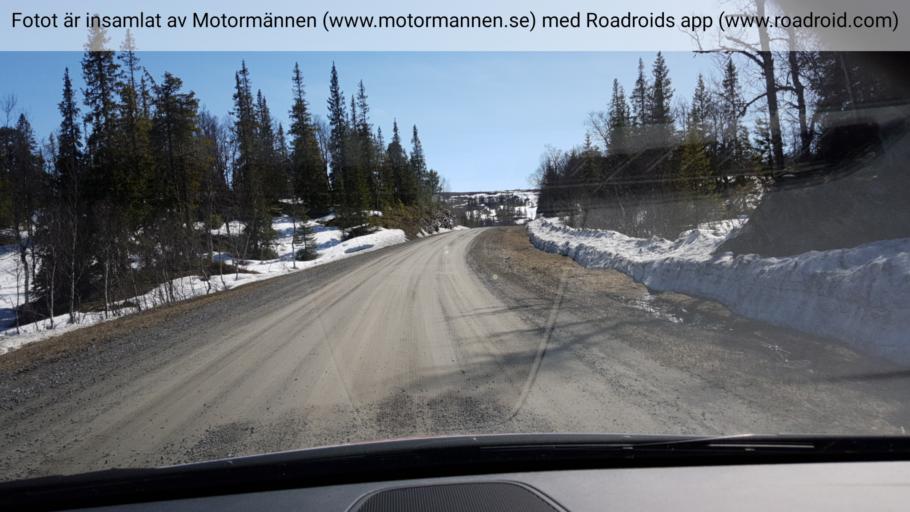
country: NO
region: Nord-Trondelag
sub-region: Snasa
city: Snaase
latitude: 63.6923
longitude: 12.3152
